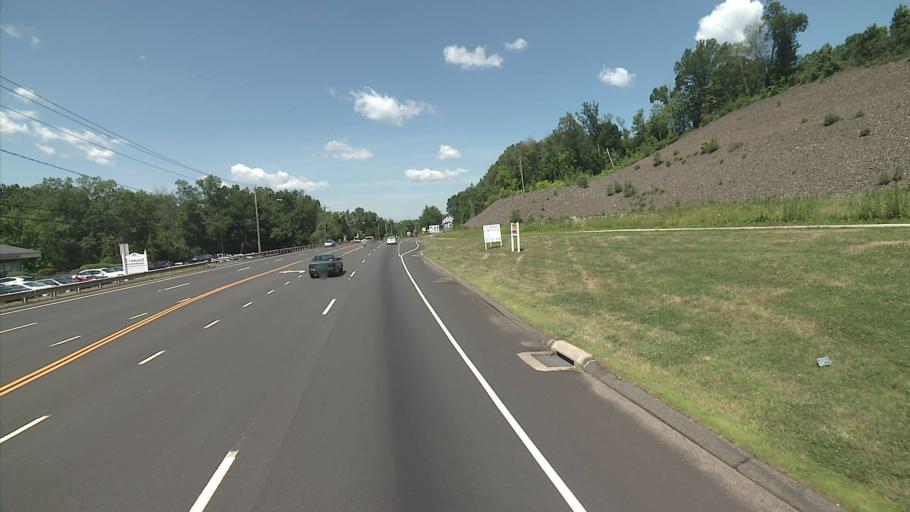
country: US
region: Connecticut
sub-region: Middlesex County
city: Cromwell
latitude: 41.6019
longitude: -72.6907
